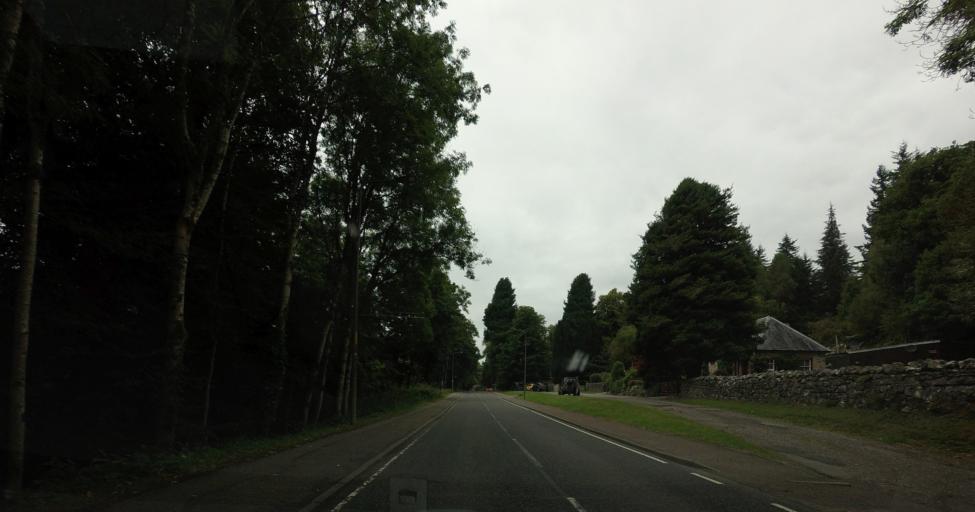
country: GB
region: Scotland
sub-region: Highland
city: Spean Bridge
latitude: 57.0689
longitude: -4.7963
